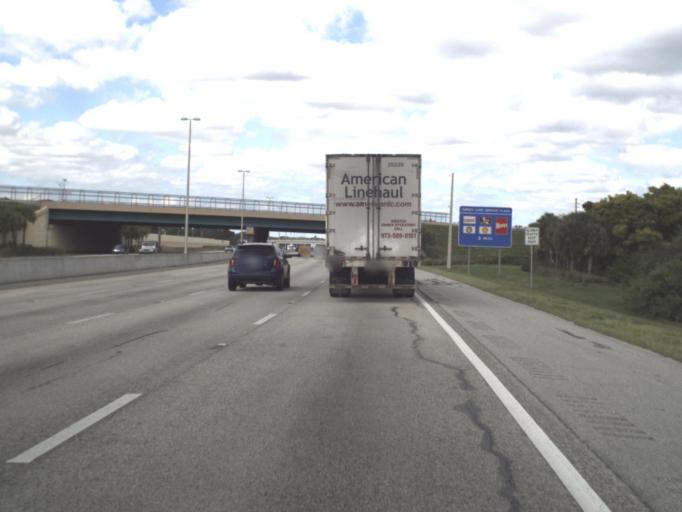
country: US
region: Florida
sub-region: Orange County
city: Tangelo Park
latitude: 28.4887
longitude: -81.4572
